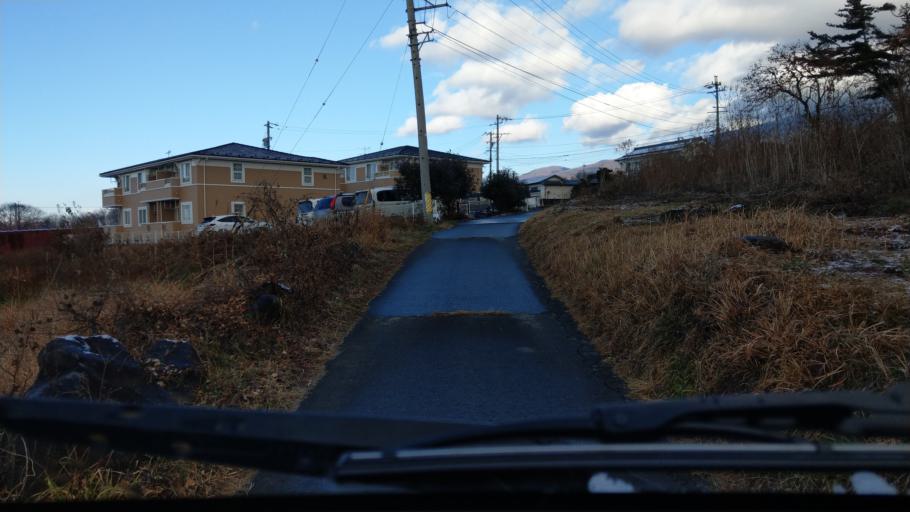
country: JP
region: Nagano
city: Komoro
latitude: 36.3493
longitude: 138.3987
